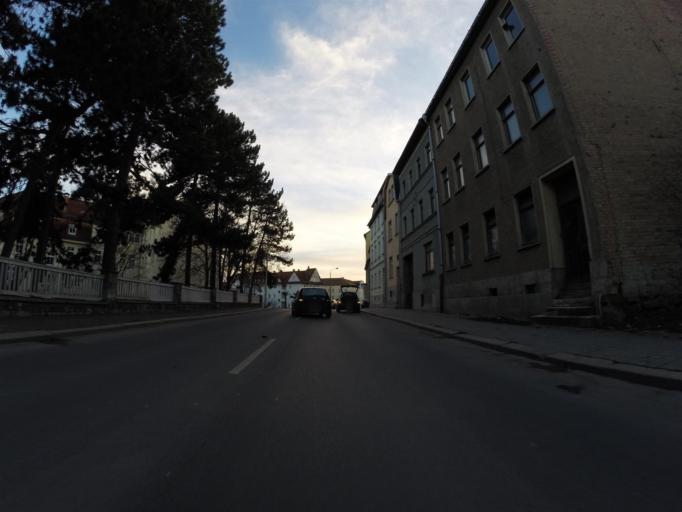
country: DE
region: Thuringia
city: Apolda
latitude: 51.0280
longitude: 11.5134
